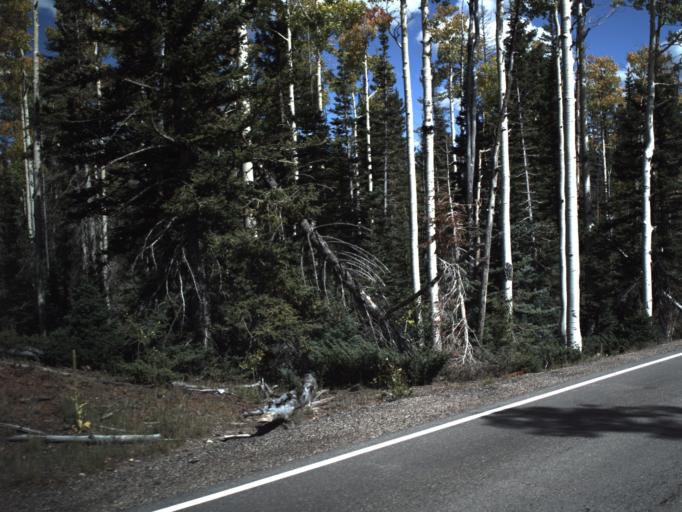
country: US
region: Utah
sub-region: Iron County
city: Parowan
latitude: 37.5222
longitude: -112.7364
